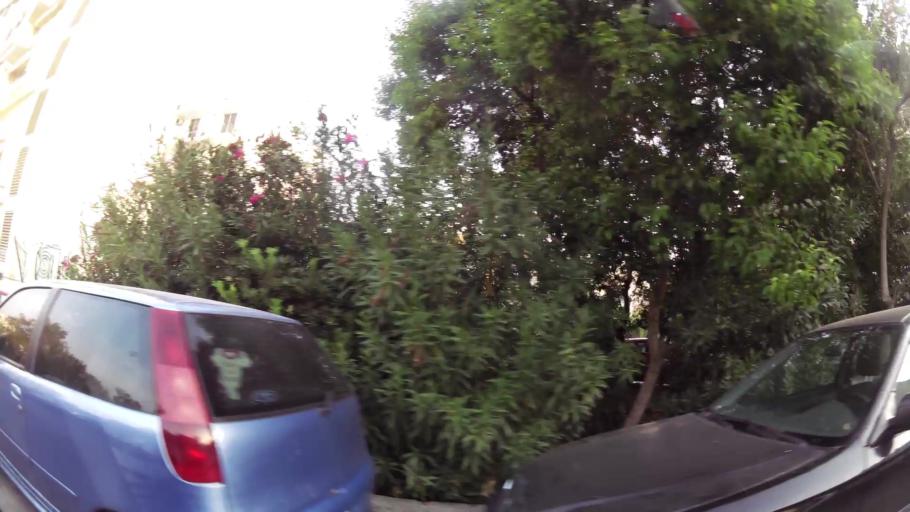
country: GR
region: Attica
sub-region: Nomarchia Athinas
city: Nea Smyrni
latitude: 37.9619
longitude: 23.7158
